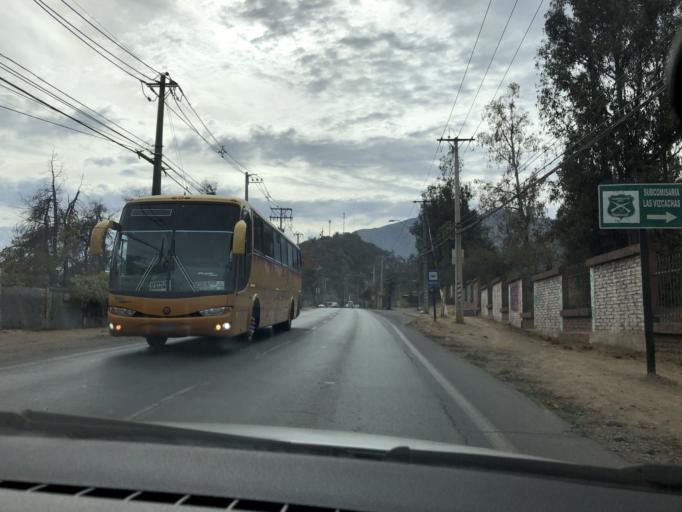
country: CL
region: Santiago Metropolitan
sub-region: Provincia de Cordillera
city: Puente Alto
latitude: -33.6009
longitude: -70.5319
